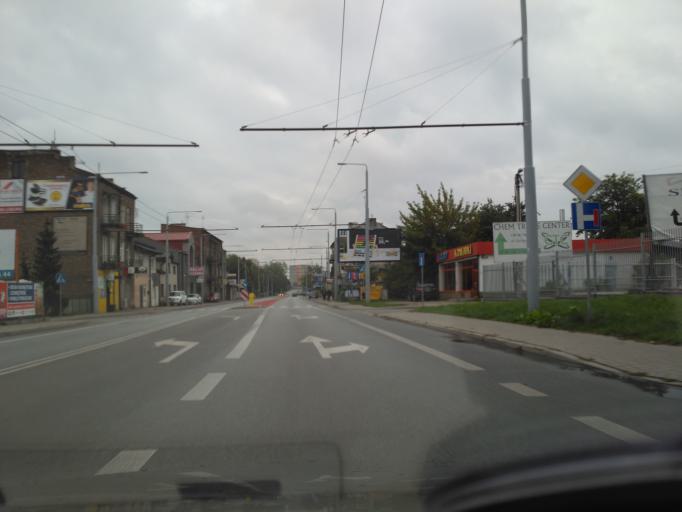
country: PL
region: Lublin Voivodeship
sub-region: Powiat lubelski
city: Lublin
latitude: 51.2393
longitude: 22.5829
